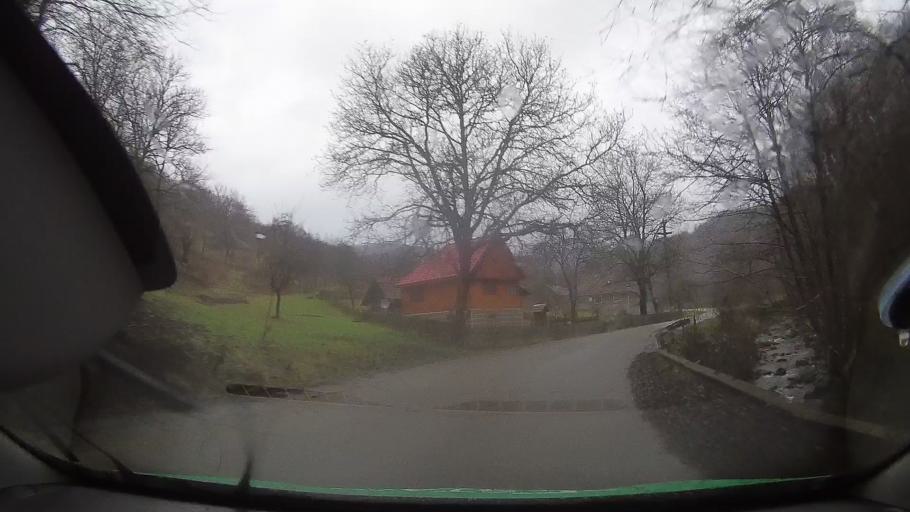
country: RO
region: Alba
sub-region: Comuna Avram Iancu
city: Avram Iancu
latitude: 46.2989
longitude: 22.7591
